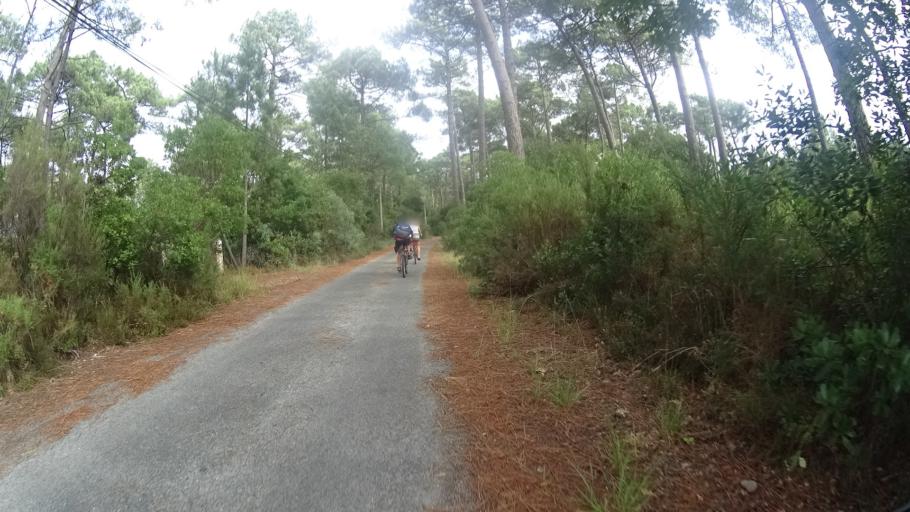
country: FR
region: Aquitaine
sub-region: Departement de la Gironde
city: Lacanau
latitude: 44.9906
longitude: -1.1431
